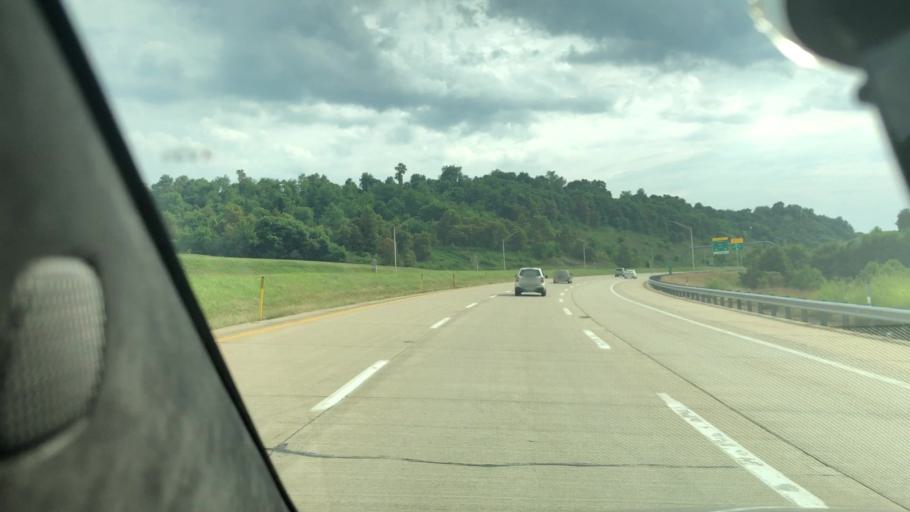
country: US
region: Pennsylvania
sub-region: Allegheny County
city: Jefferson Hills
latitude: 40.2850
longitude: -79.9188
